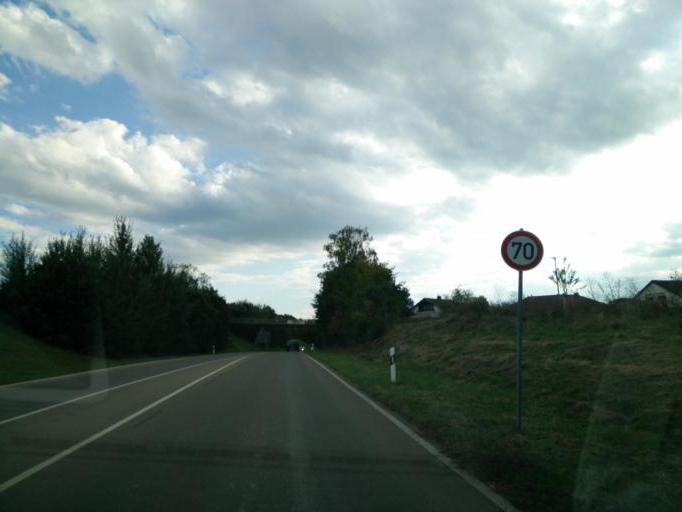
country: DE
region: Baden-Wuerttemberg
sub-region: Tuebingen Region
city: Kirchentellinsfurt
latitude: 48.5304
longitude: 9.1583
